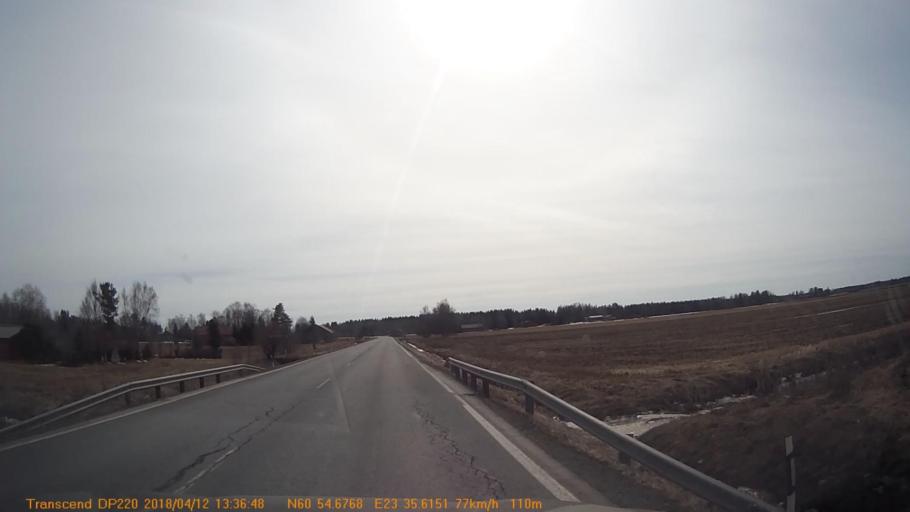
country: FI
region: Haeme
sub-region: Forssa
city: Forssa
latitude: 60.9110
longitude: 23.5935
